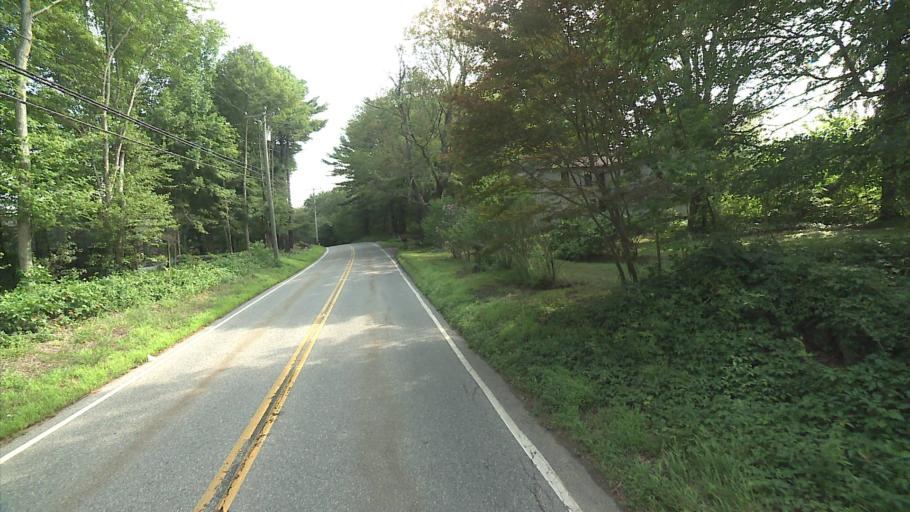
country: US
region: Connecticut
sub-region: Middlesex County
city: Moodus
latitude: 41.5574
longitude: -72.4077
